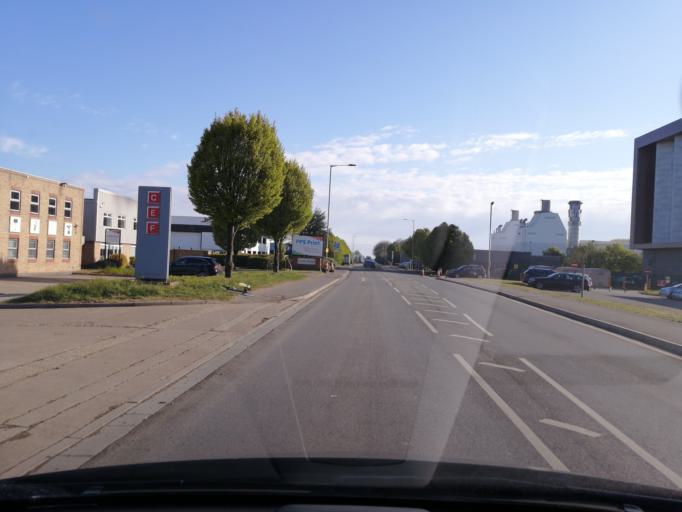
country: GB
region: England
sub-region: Peterborough
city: Eye
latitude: 52.5749
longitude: -0.2085
